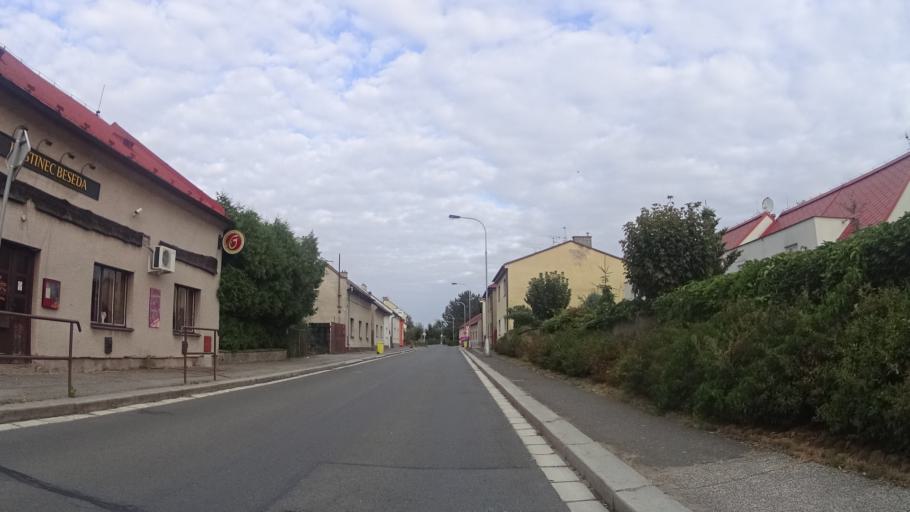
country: CZ
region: Kralovehradecky
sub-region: Okres Hradec Kralove
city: Hradec Kralove
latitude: 50.2070
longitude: 15.7933
